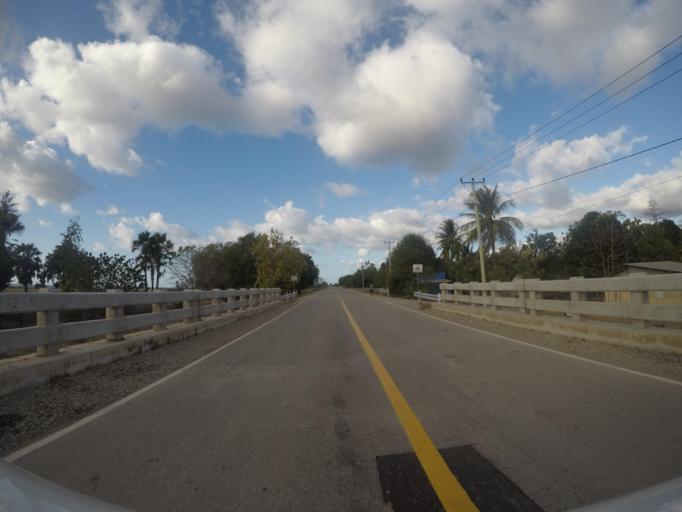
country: TL
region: Lautem
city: Lospalos
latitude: -8.3995
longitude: 126.8327
